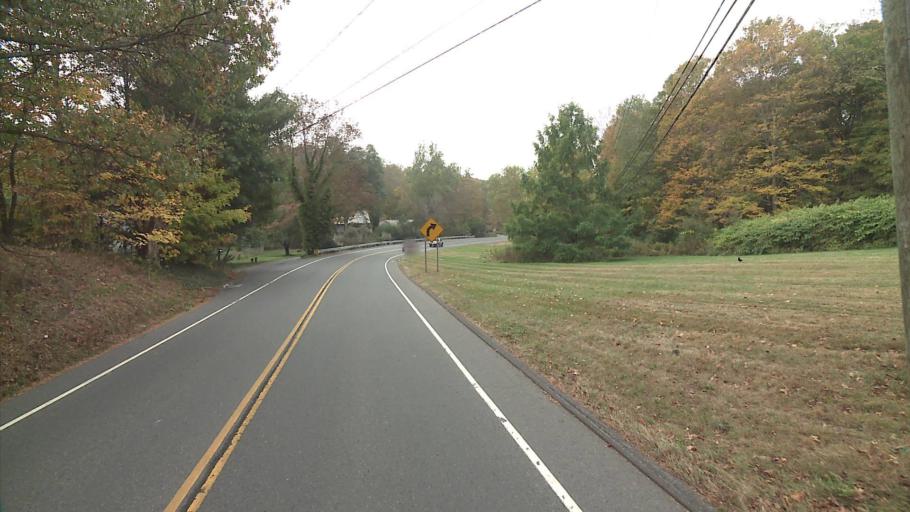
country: US
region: Connecticut
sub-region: Litchfield County
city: Woodbury Center
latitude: 41.5785
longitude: -73.1753
